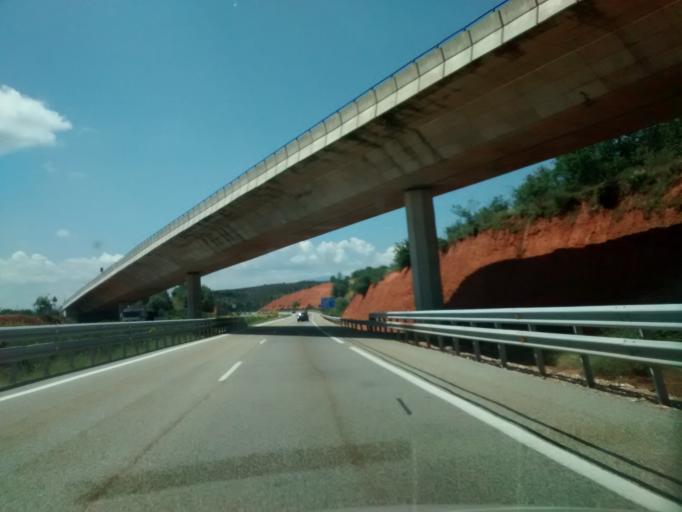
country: ES
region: Castille and Leon
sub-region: Provincia de Leon
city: Brazuelo
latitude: 42.5000
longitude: -6.1227
